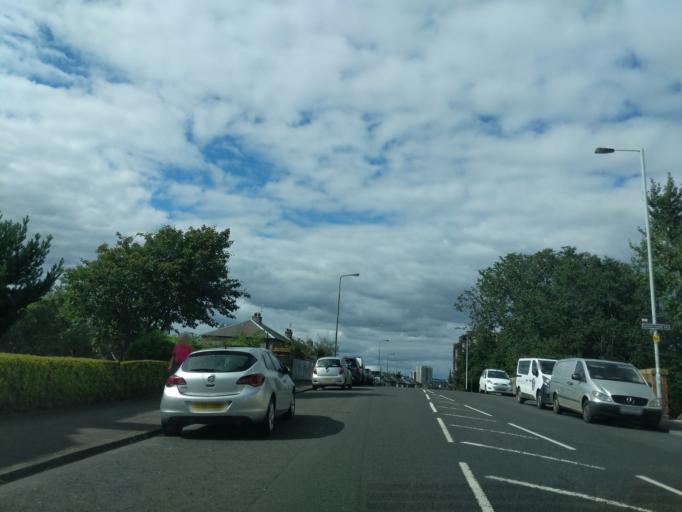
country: GB
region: Scotland
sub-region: West Lothian
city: Seafield
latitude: 55.9638
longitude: -3.1614
